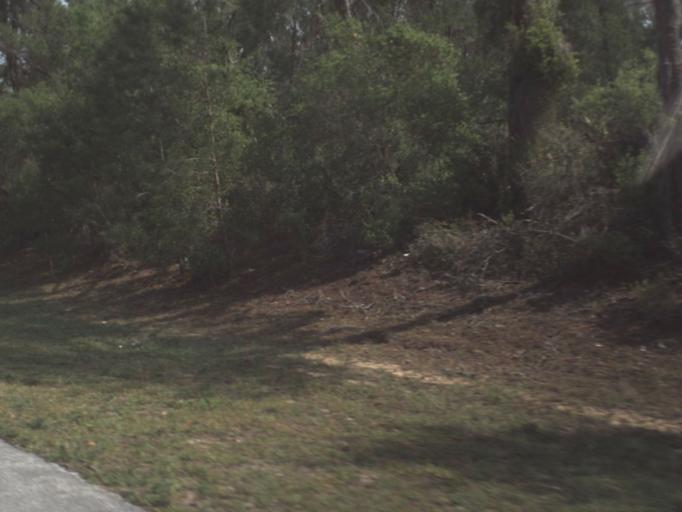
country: US
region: Florida
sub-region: Lake County
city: Astor
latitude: 29.2646
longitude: -81.6465
